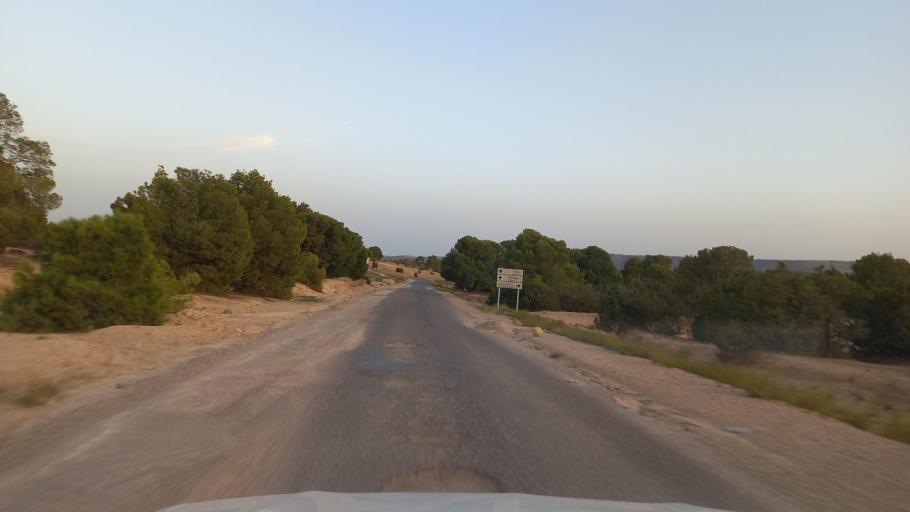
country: TN
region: Al Qasrayn
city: Sbiba
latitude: 35.4157
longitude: 8.9262
